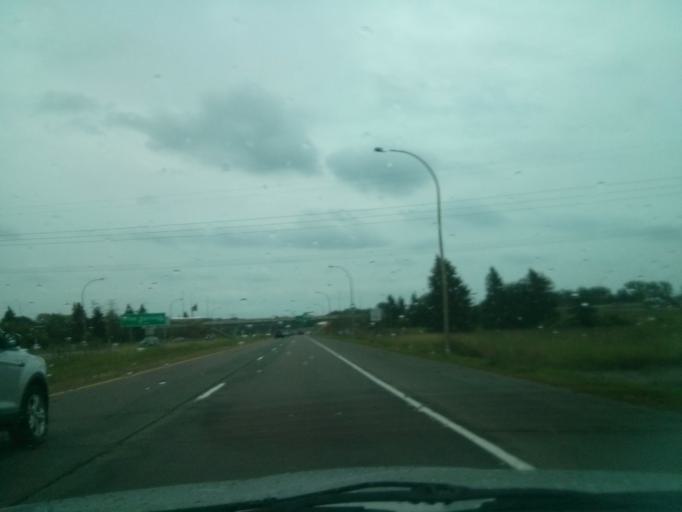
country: US
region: Minnesota
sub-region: Ramsey County
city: North Saint Paul
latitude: 45.0289
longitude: -92.9654
